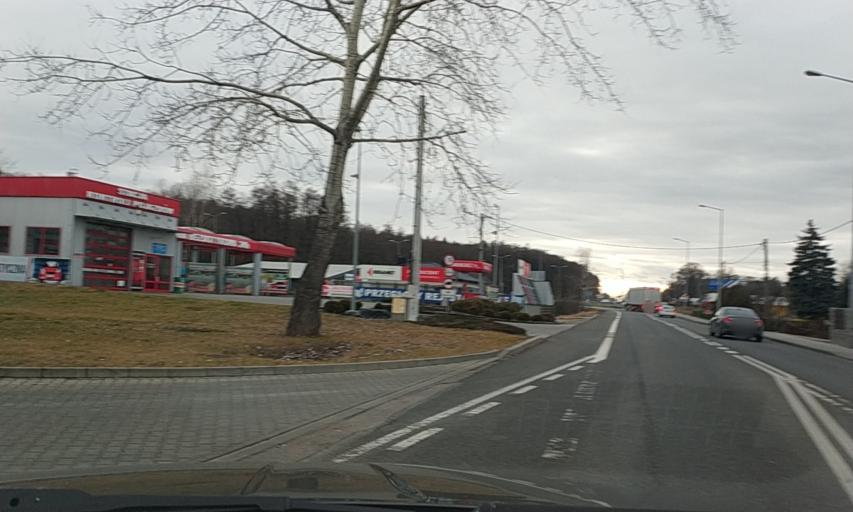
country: PL
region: Lesser Poland Voivodeship
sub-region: Powiat tarnowski
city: Koszyce Wielkie
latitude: 49.9913
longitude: 20.9352
